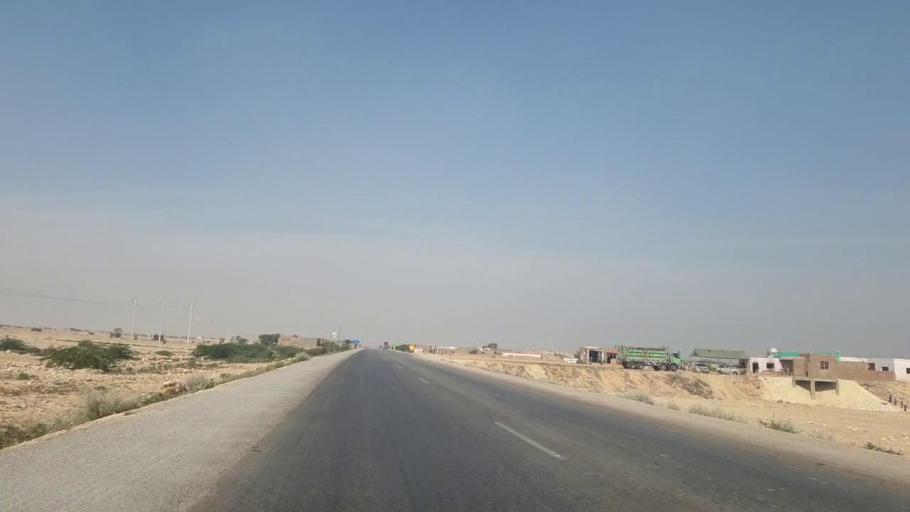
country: PK
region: Sindh
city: Hala
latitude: 25.7895
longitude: 68.2816
